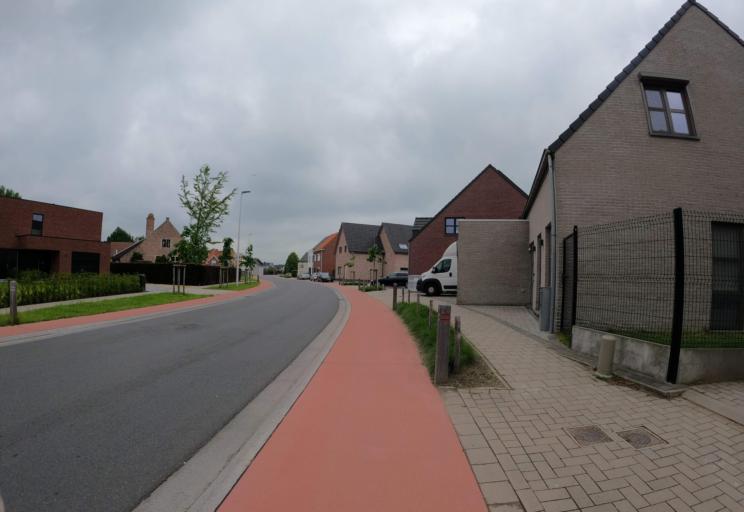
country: BE
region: Flanders
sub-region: Provincie Oost-Vlaanderen
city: Zele
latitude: 51.0459
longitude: 4.0333
